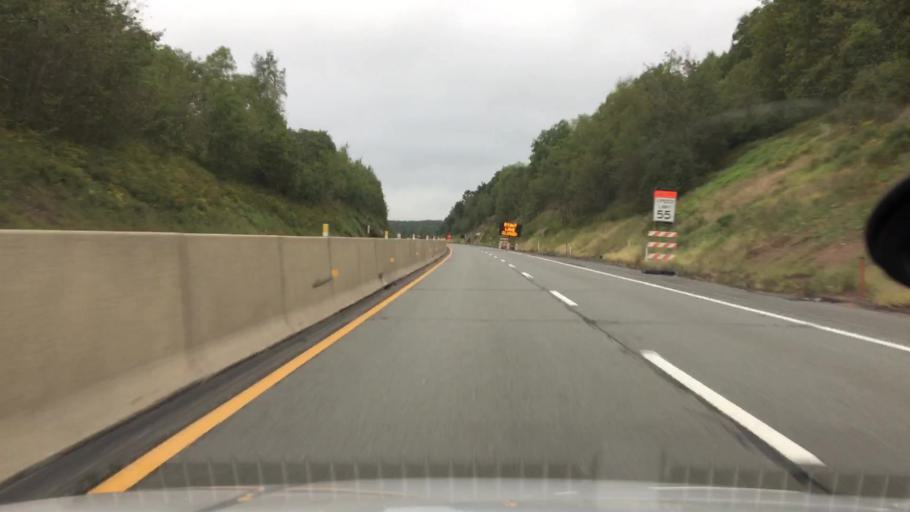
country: US
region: Pennsylvania
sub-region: Luzerne County
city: White Haven
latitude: 41.1074
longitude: -75.7523
